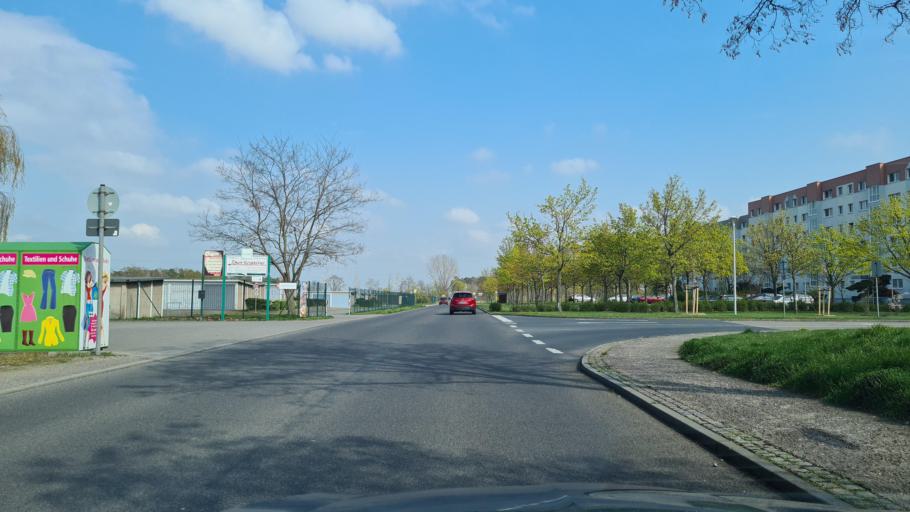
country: DE
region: Saxony
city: Nauwalde
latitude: 51.4136
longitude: 13.4575
